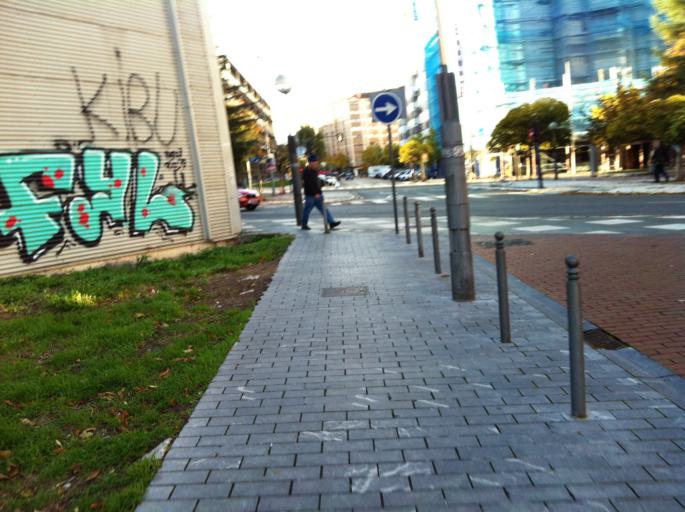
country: ES
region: Basque Country
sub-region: Provincia de Alava
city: Gasteiz / Vitoria
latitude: 42.8432
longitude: -2.6803
